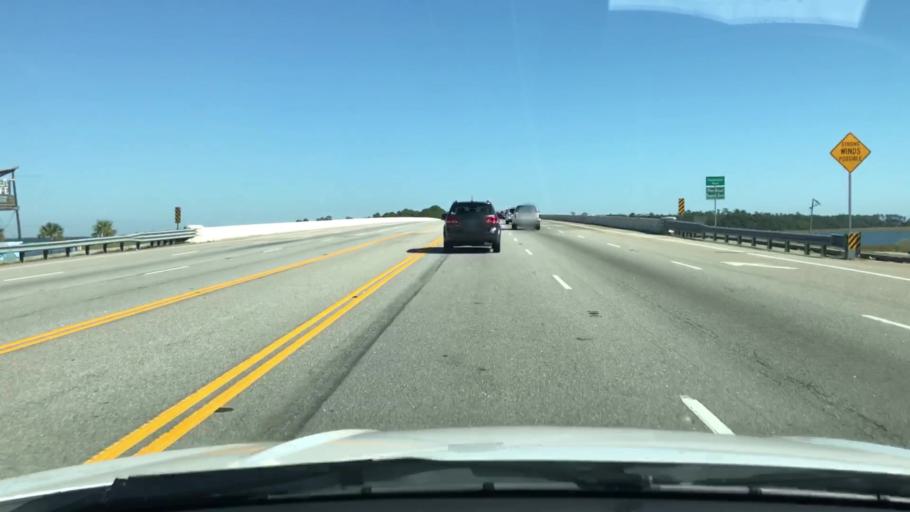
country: US
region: South Carolina
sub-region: Beaufort County
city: Laurel Bay
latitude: 32.3740
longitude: -80.8384
